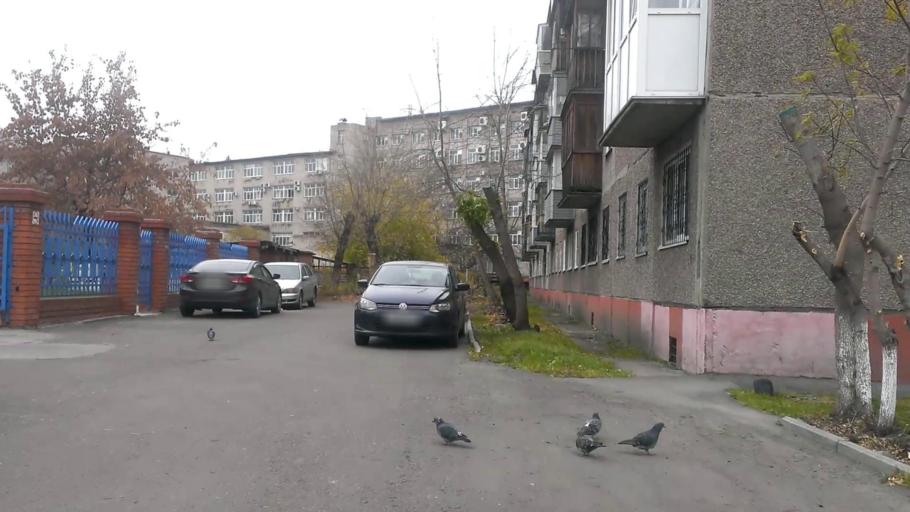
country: RU
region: Altai Krai
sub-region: Gorod Barnaulskiy
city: Barnaul
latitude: 53.3480
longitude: 83.7709
